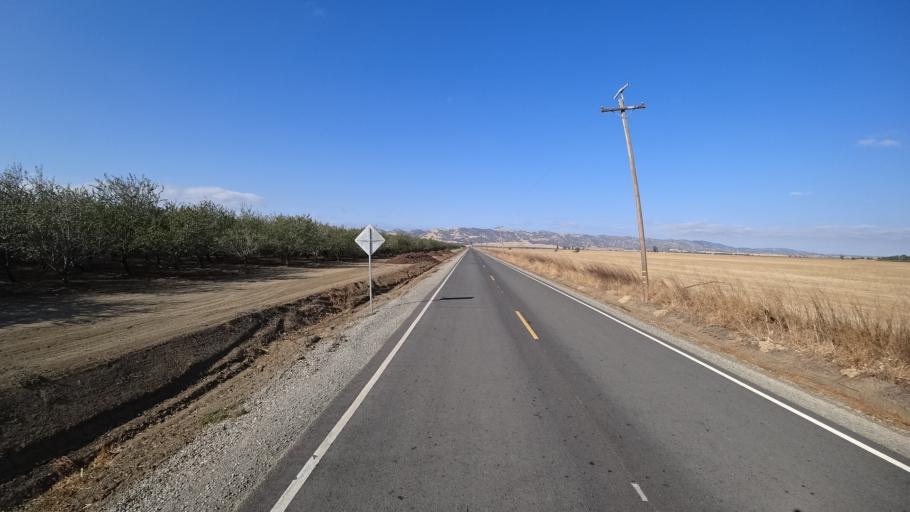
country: US
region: California
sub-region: Yolo County
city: Esparto
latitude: 38.7811
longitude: -122.0274
